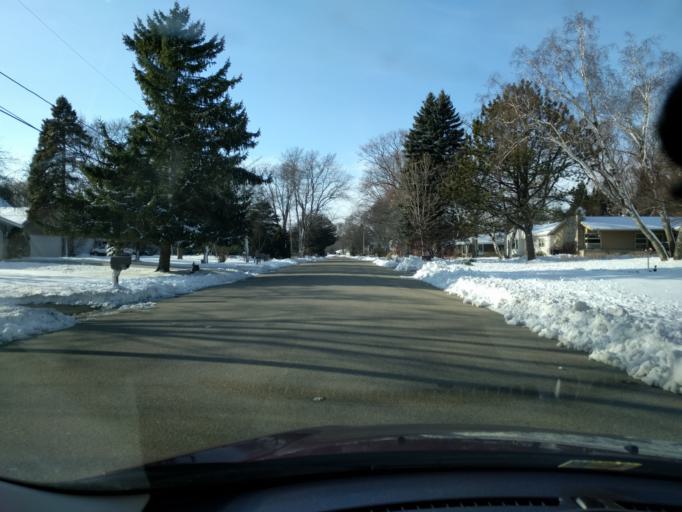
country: US
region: Wisconsin
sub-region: Milwaukee County
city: Glendale
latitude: 43.1262
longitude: -87.9172
